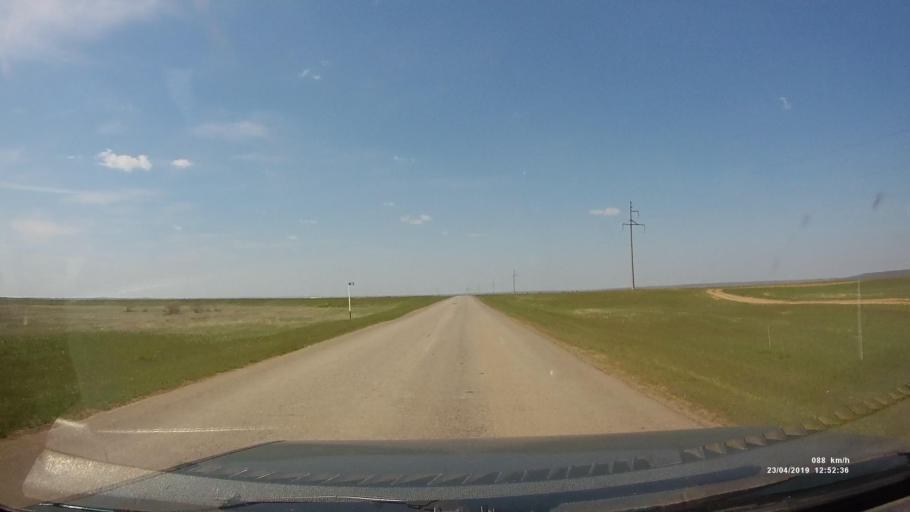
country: RU
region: Kalmykiya
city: Yashalta
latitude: 46.5662
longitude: 42.6073
